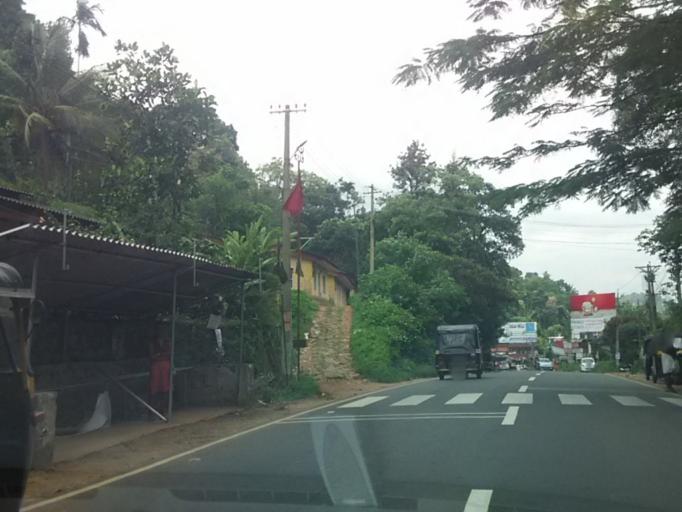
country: IN
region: Kerala
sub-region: Wayanad
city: Kalpetta
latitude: 11.5491
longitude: 76.0389
